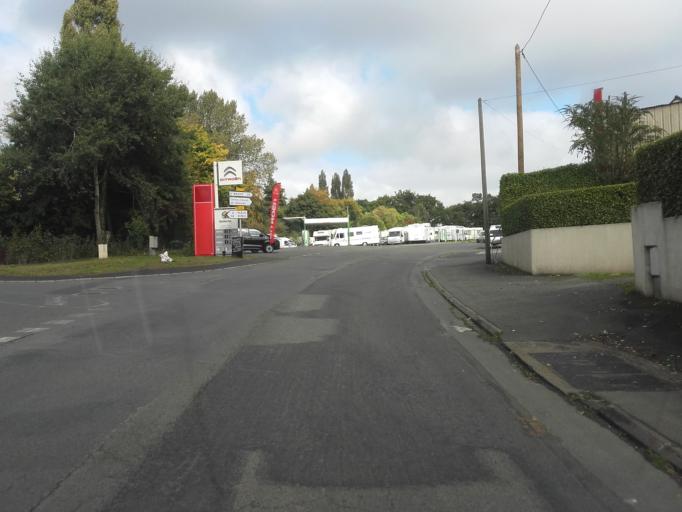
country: FR
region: Brittany
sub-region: Departement des Cotes-d'Armor
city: Plelo
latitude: 48.5447
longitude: -2.9651
